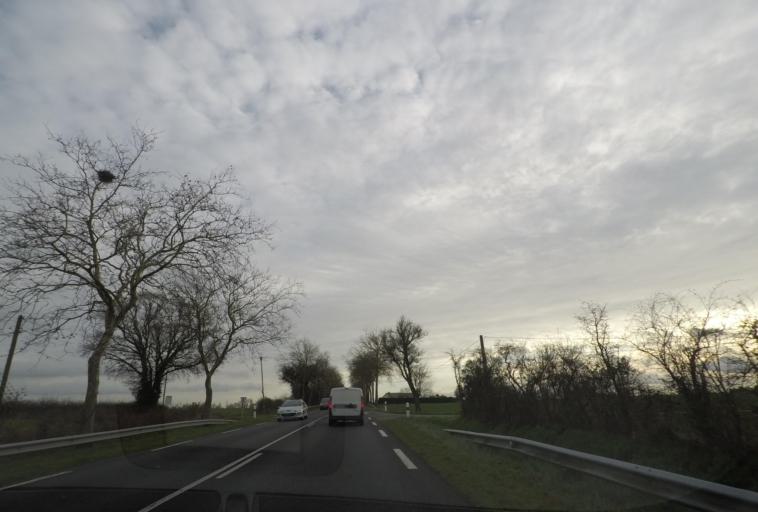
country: FR
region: Centre
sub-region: Departement du Loir-et-Cher
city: Sarge-sur-Braye
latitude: 47.9064
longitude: 0.8762
